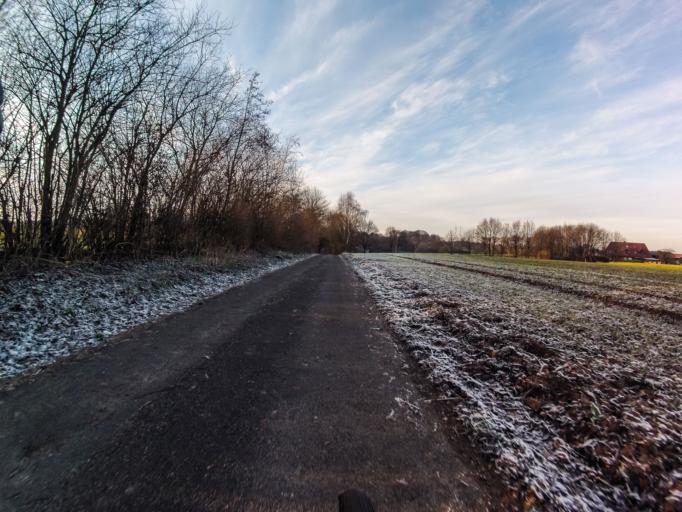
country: DE
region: North Rhine-Westphalia
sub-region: Regierungsbezirk Munster
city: Mettingen
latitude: 52.2861
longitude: 7.8002
